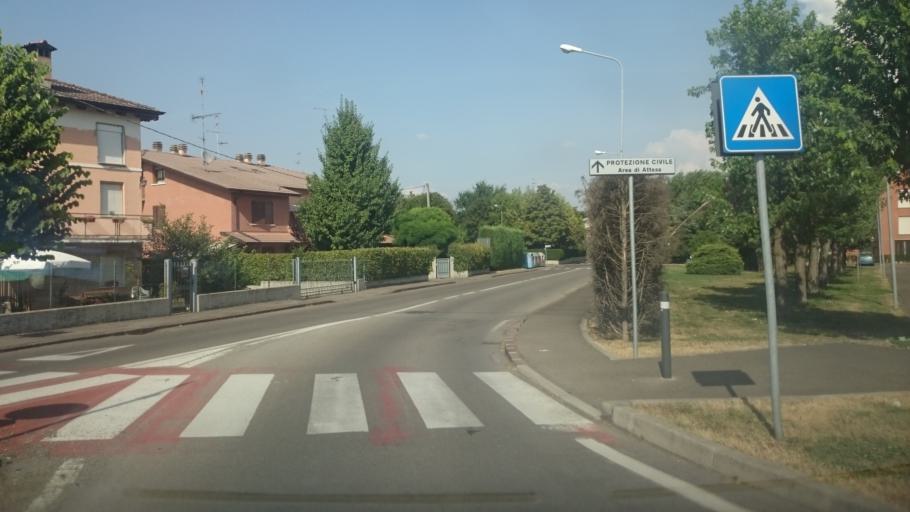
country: IT
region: Emilia-Romagna
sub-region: Provincia di Reggio Emilia
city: Rubiera
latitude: 44.6495
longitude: 10.7736
